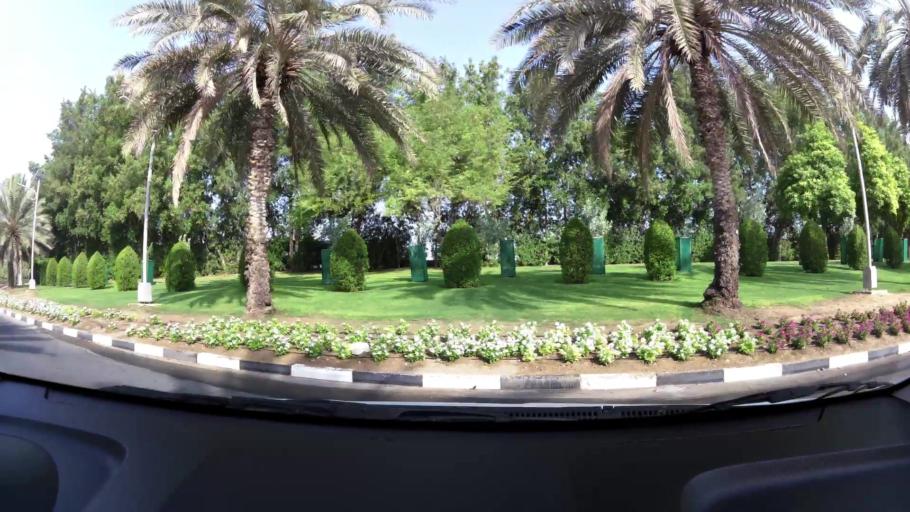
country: AE
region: Ash Shariqah
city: Sharjah
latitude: 25.3167
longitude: 55.3494
